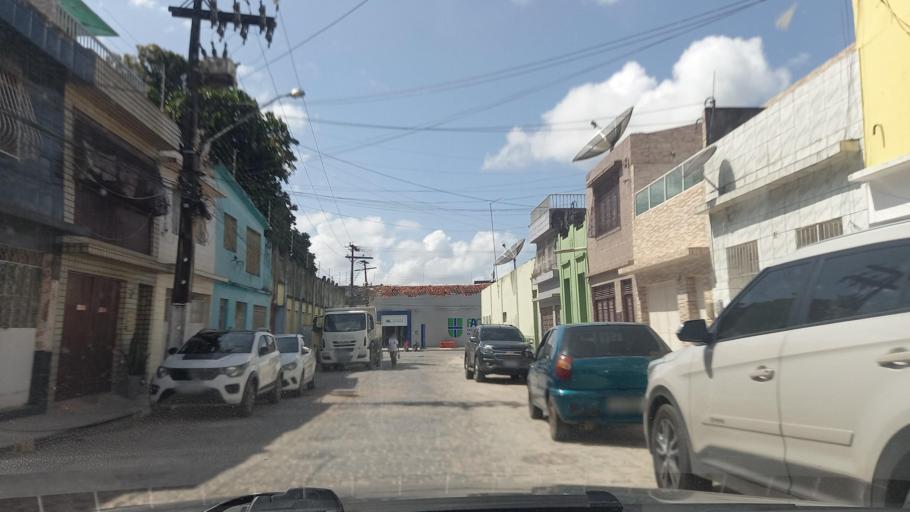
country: BR
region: Pernambuco
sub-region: Goiana
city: Goiana
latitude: -7.5598
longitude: -34.9954
